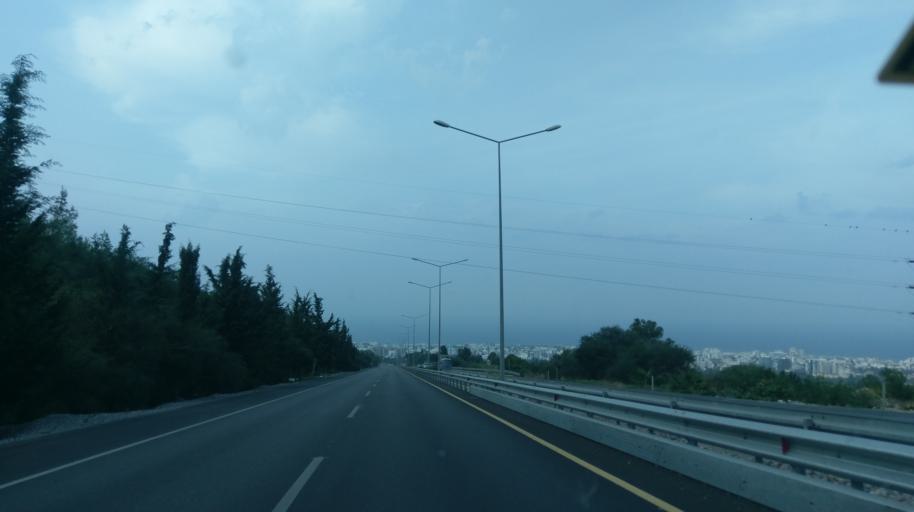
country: CY
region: Keryneia
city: Kyrenia
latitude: 35.3127
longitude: 33.3238
